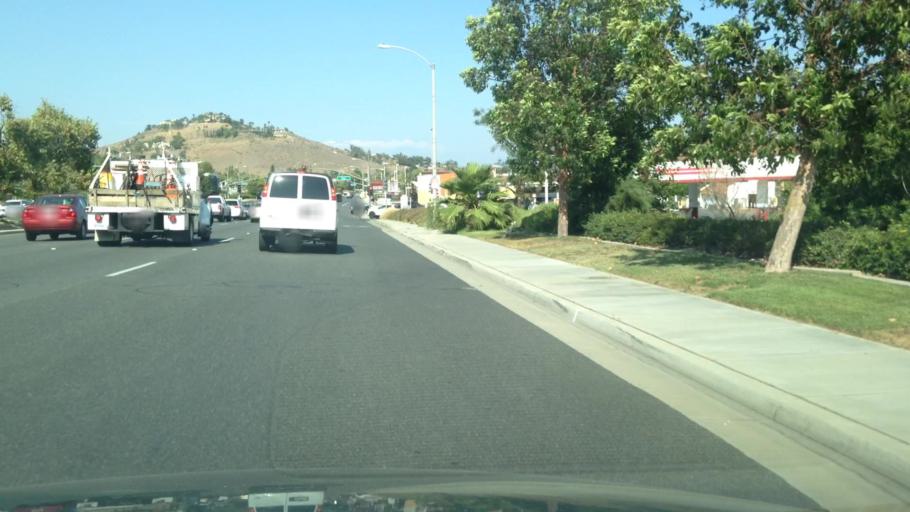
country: US
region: California
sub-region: Riverside County
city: Pedley
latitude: 33.9767
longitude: -117.4637
